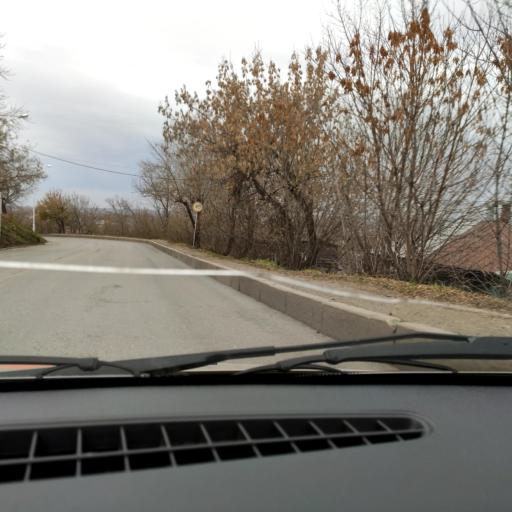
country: RU
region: Bashkortostan
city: Ufa
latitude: 54.7407
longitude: 55.9365
